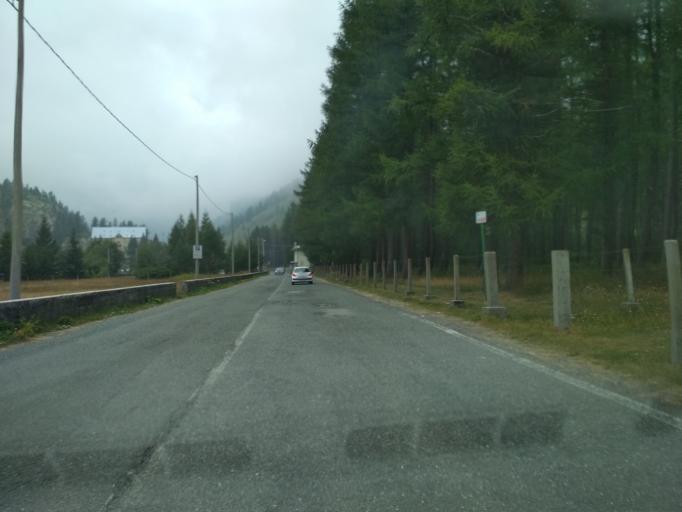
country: IT
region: Piedmont
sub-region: Provincia di Torino
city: Balme
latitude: 45.3023
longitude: 7.1904
